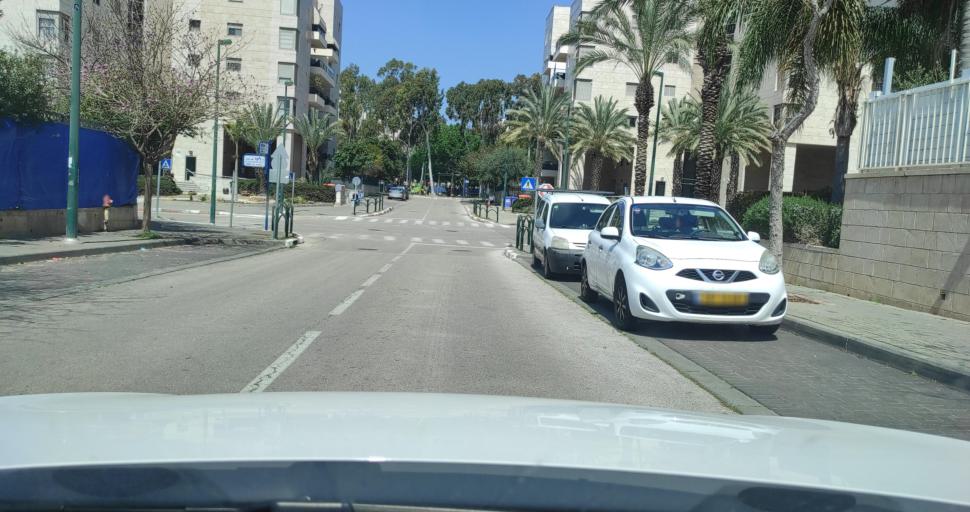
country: IL
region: Central District
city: Nordiyya
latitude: 32.3000
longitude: 34.8715
